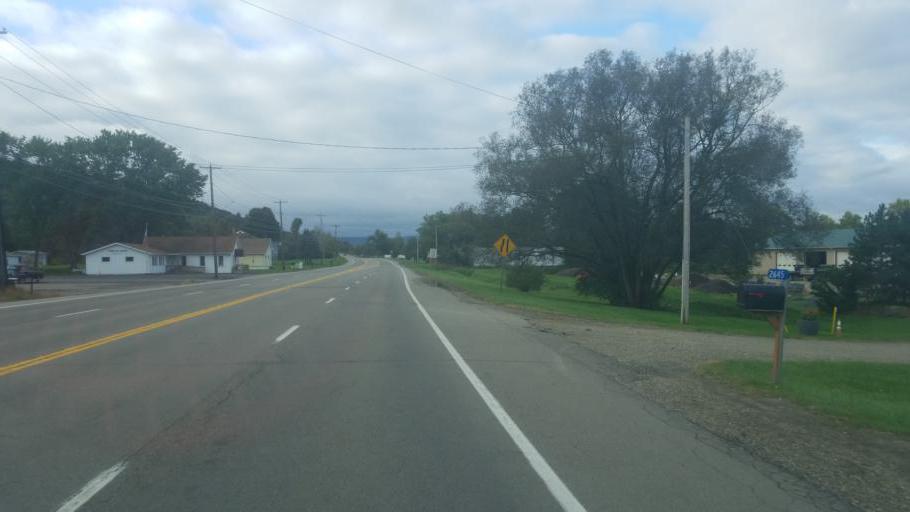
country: US
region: New York
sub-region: Cattaraugus County
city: Olean
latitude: 42.1138
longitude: -78.4158
